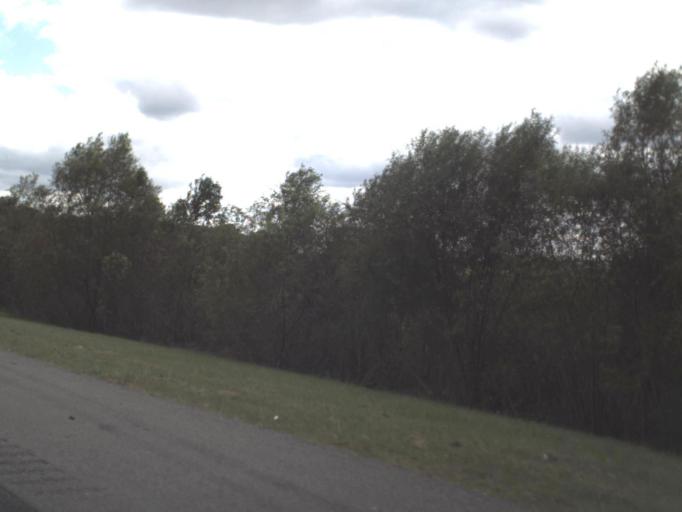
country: US
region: Florida
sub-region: Orange County
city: Oakland
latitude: 28.5459
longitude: -81.6182
